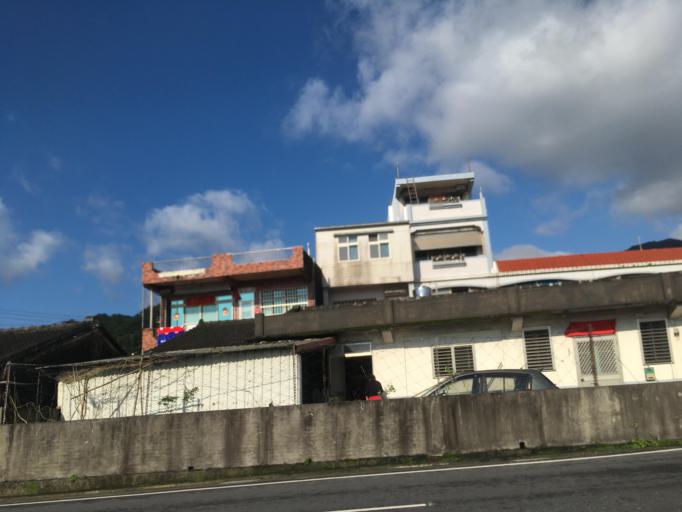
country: TW
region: Taiwan
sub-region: Yilan
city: Yilan
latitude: 24.9016
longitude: 121.8635
